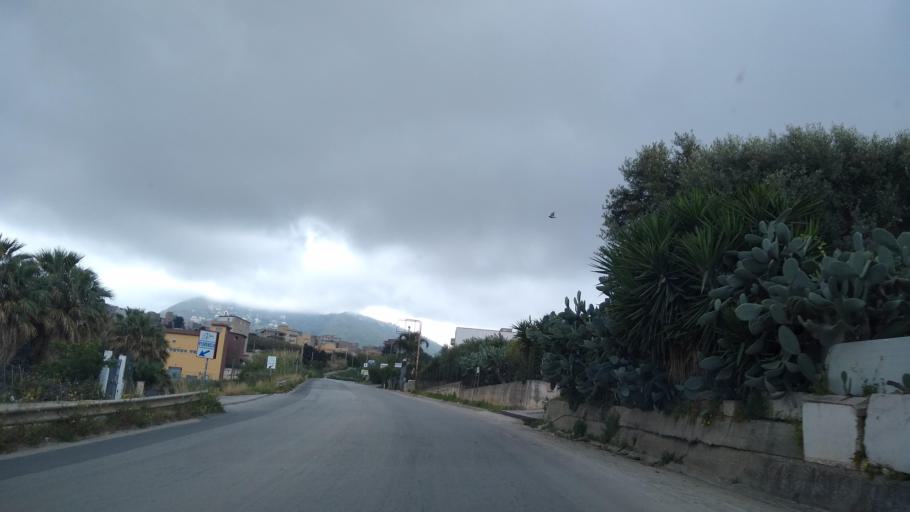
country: IT
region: Sicily
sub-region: Trapani
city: Alcamo
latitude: 37.9893
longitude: 12.9528
